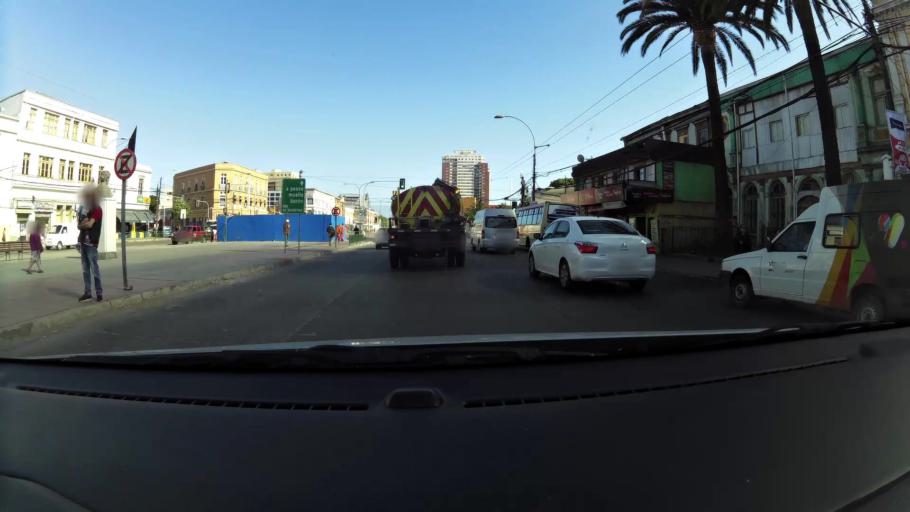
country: CL
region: Valparaiso
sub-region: Provincia de Valparaiso
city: Valparaiso
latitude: -33.0516
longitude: -71.6021
